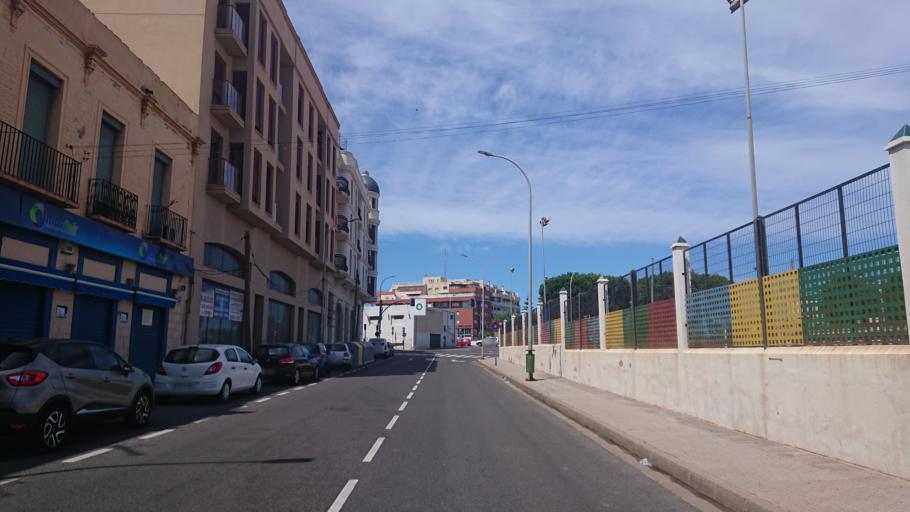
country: ES
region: Melilla
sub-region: Melilla
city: Melilla
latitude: 35.2855
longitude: -2.9416
